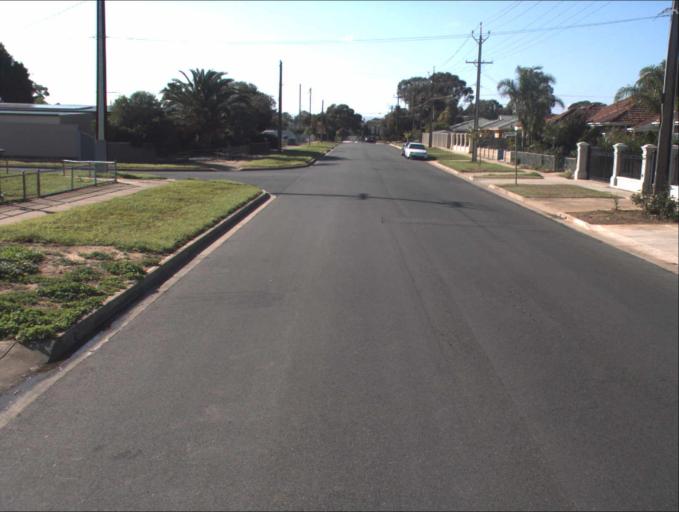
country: AU
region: South Australia
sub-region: Charles Sturt
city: Woodville North
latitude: -34.8587
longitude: 138.5502
